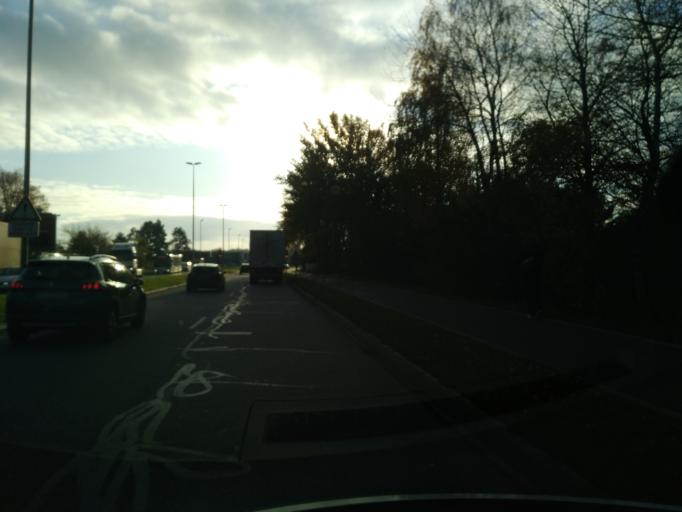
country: FR
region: Ile-de-France
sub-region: Departement des Yvelines
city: Trappes
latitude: 48.7737
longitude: 2.0142
